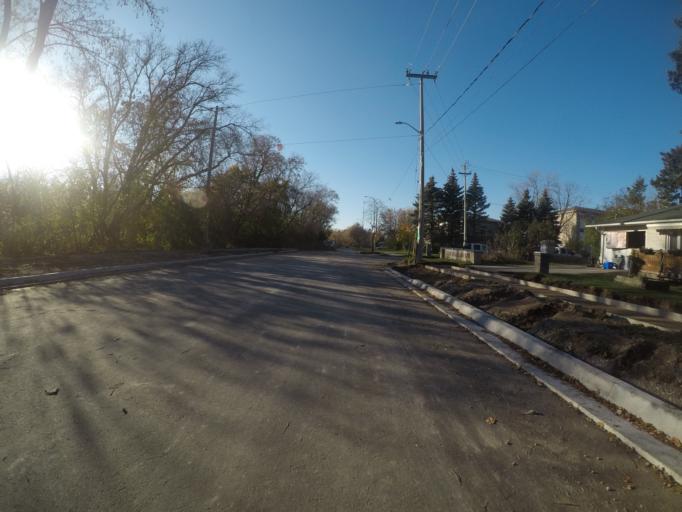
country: CA
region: Ontario
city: Kitchener
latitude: 43.4319
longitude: -80.4566
